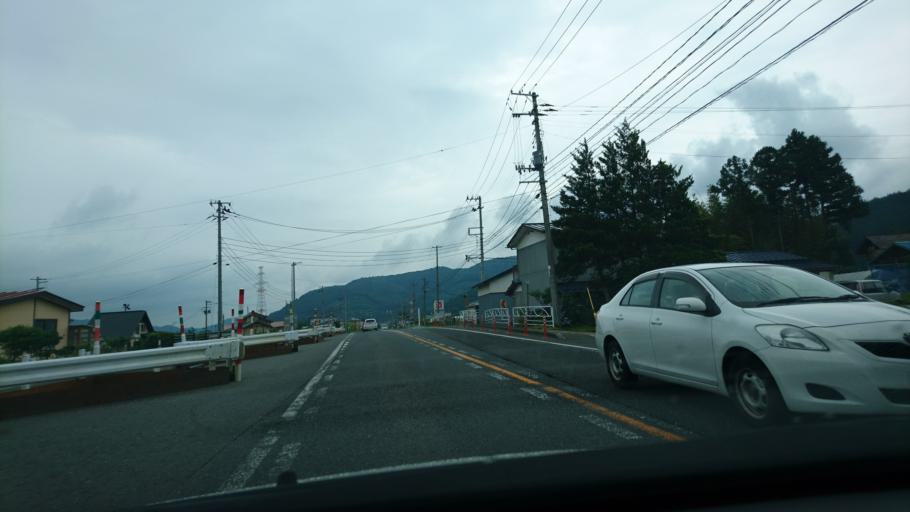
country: JP
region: Miyagi
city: Furukawa
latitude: 38.7359
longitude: 140.7491
